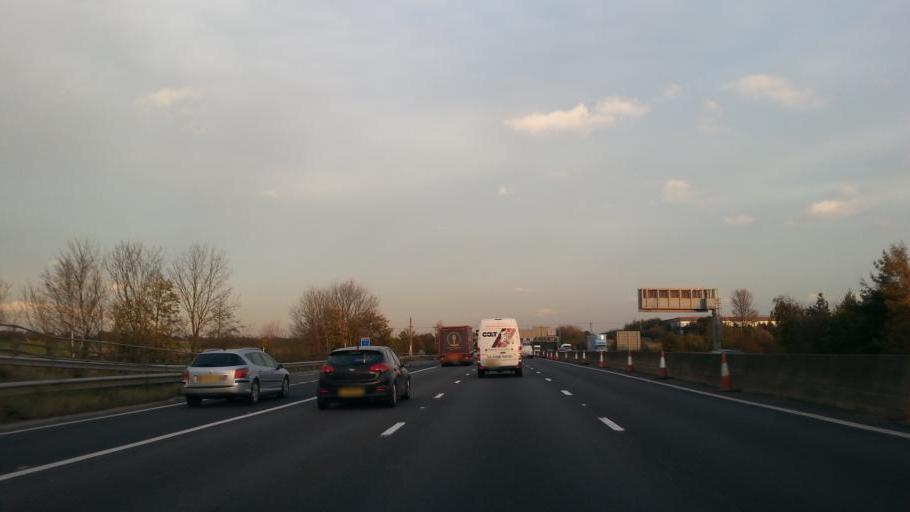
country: GB
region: England
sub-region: City and Borough of Leeds
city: Lofthouse
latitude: 53.7282
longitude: -1.4810
